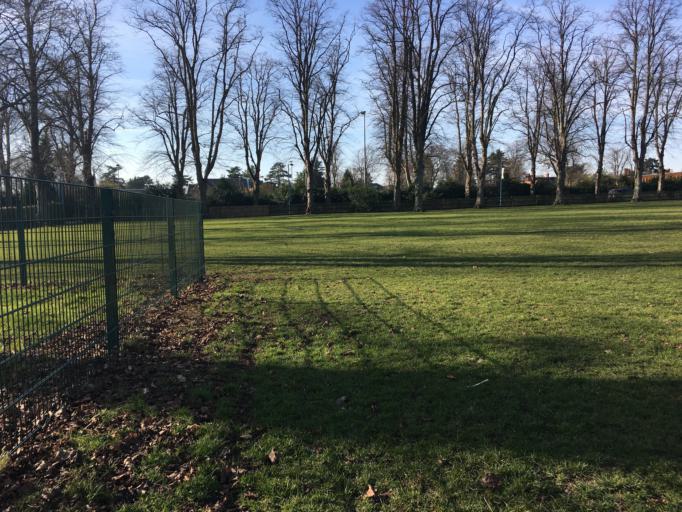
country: GB
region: England
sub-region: Warwickshire
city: Rugby
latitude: 52.3674
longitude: -1.2542
